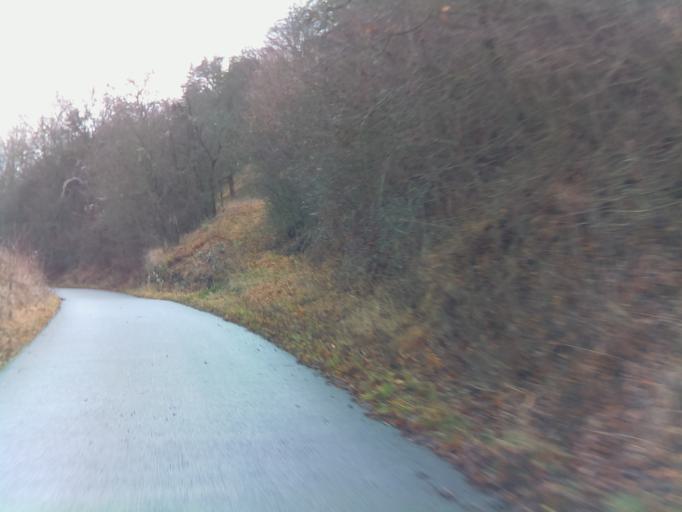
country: DE
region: Thuringia
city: Reinstadt
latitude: 50.7859
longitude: 11.4697
